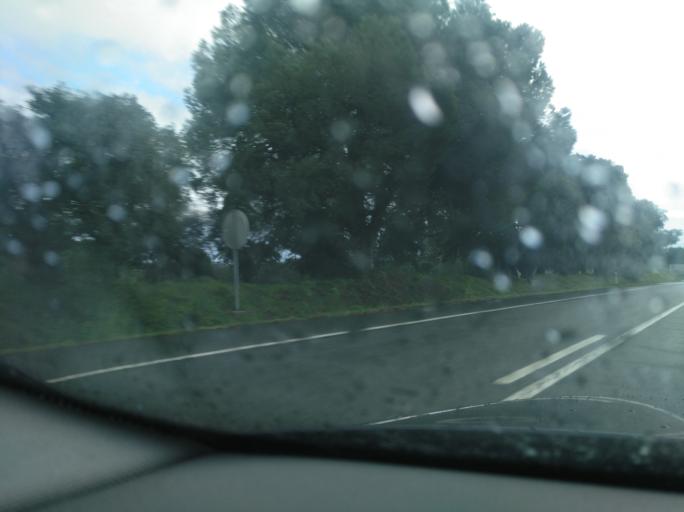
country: PT
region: Setubal
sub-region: Grandola
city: Grandola
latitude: 38.0799
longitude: -8.4170
